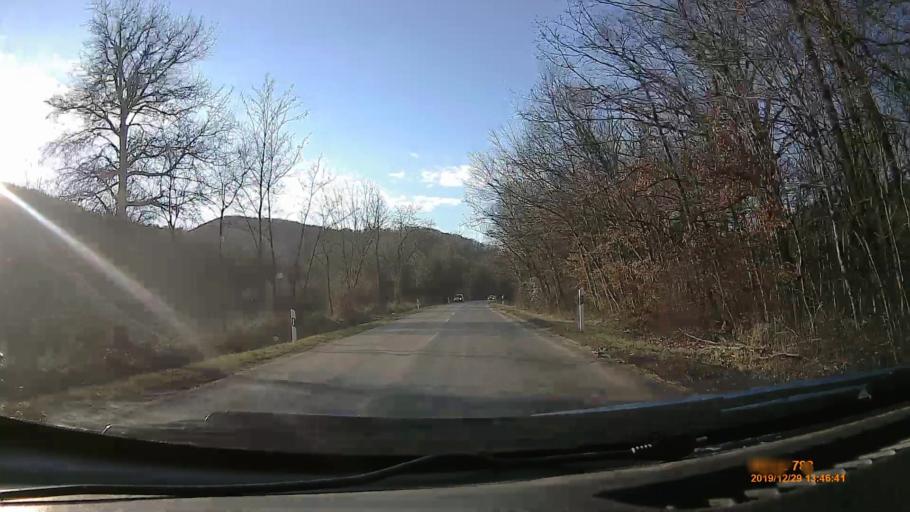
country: HU
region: Heves
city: Matraderecske
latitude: 47.9244
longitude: 20.0743
